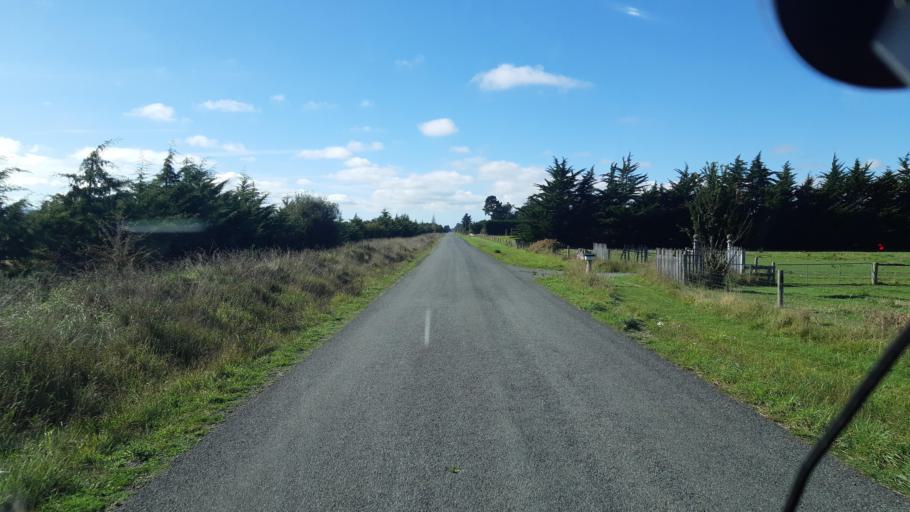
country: NZ
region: Canterbury
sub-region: Waimakariri District
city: Woodend
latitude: -43.2664
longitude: 172.4991
